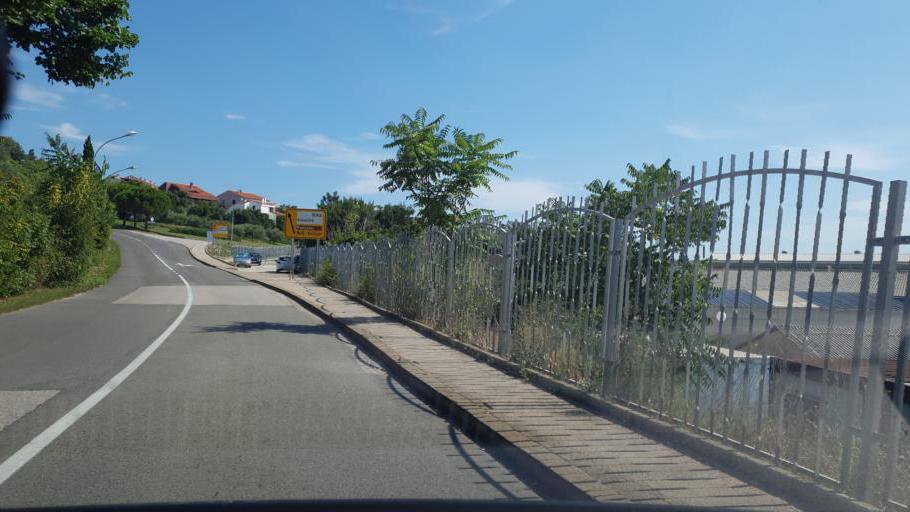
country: HR
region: Primorsko-Goranska
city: Punat
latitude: 45.0270
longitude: 14.6303
